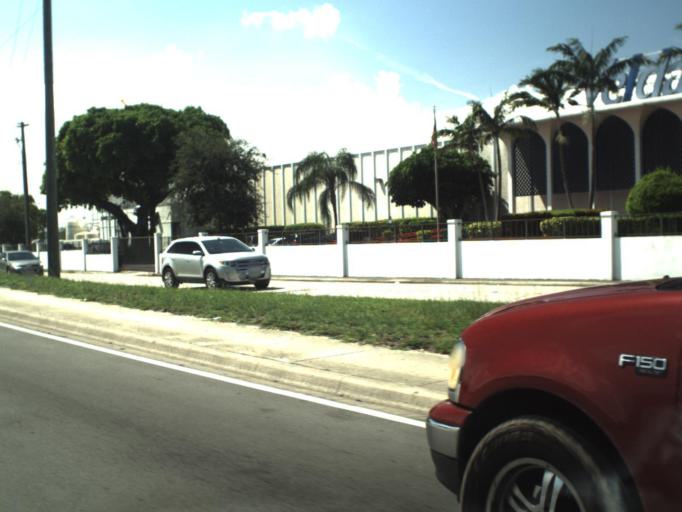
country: US
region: Florida
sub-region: Miami-Dade County
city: Norland
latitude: 25.9415
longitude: -80.1906
